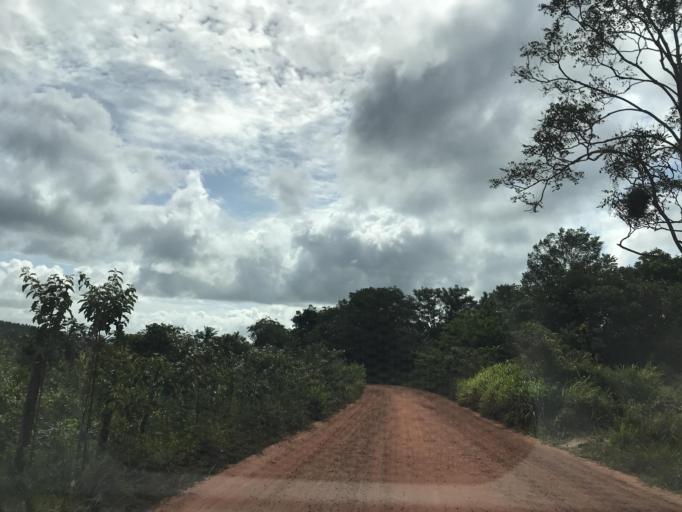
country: BR
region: Bahia
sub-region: Entre Rios
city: Entre Rios
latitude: -12.1708
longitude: -38.1497
